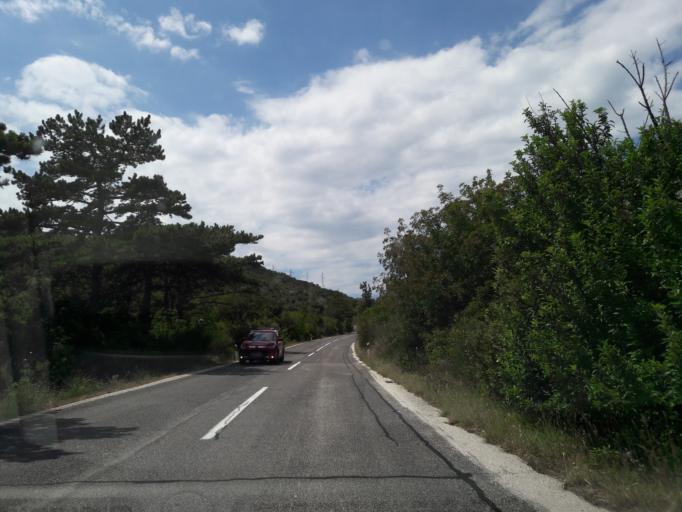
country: HR
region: Dubrovacko-Neretvanska
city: Orebic
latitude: 42.9689
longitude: 17.2847
